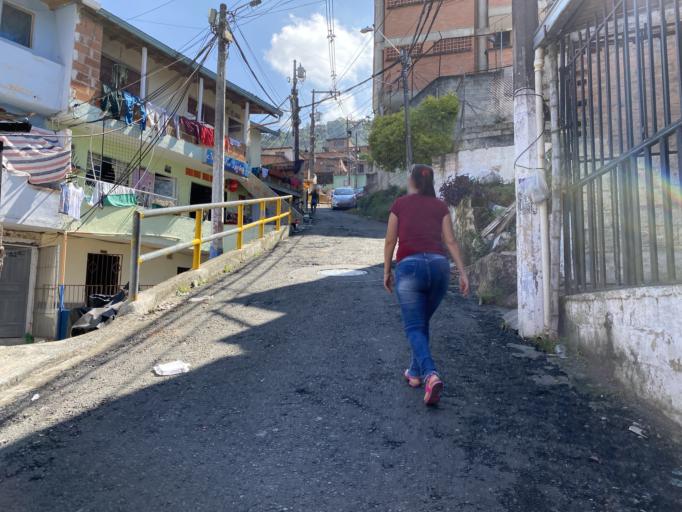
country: CO
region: Antioquia
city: Bello
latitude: 6.2974
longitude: -75.5496
